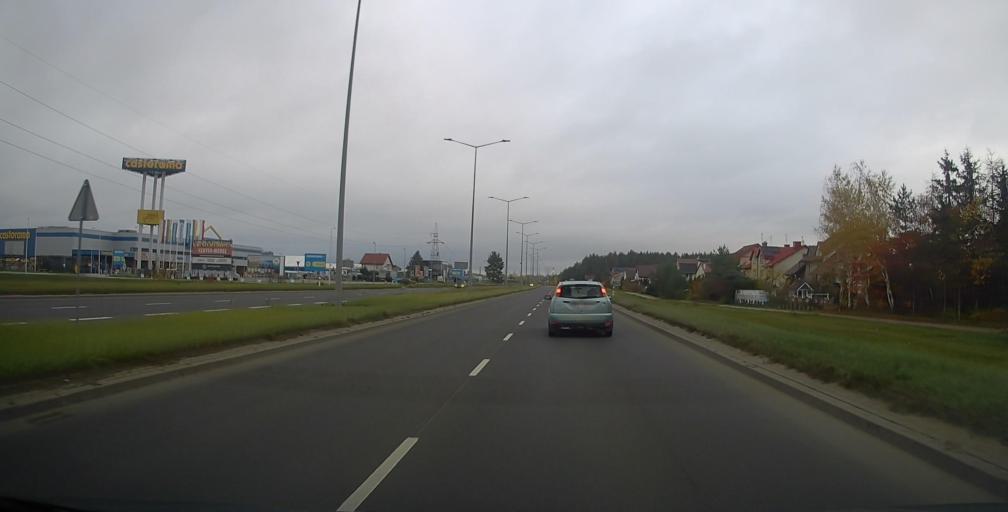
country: PL
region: Warmian-Masurian Voivodeship
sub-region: Powiat elcki
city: Elk
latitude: 53.8119
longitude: 22.3797
